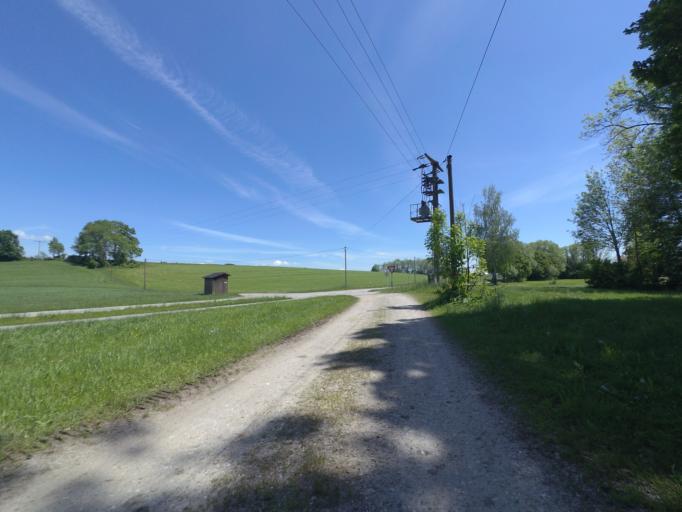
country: DE
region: Bavaria
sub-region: Upper Bavaria
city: Petting
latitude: 47.9478
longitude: 12.7908
